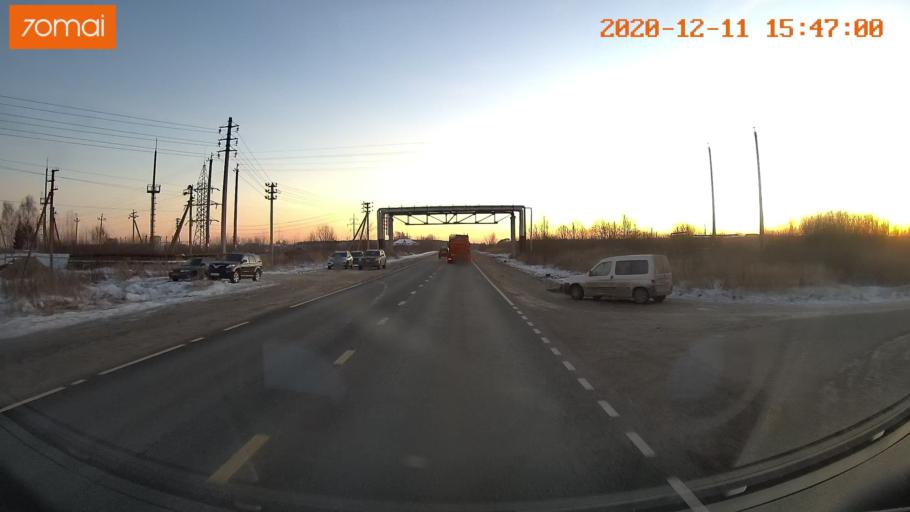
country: RU
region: Ivanovo
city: Novo-Talitsy
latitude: 57.0017
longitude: 40.8553
